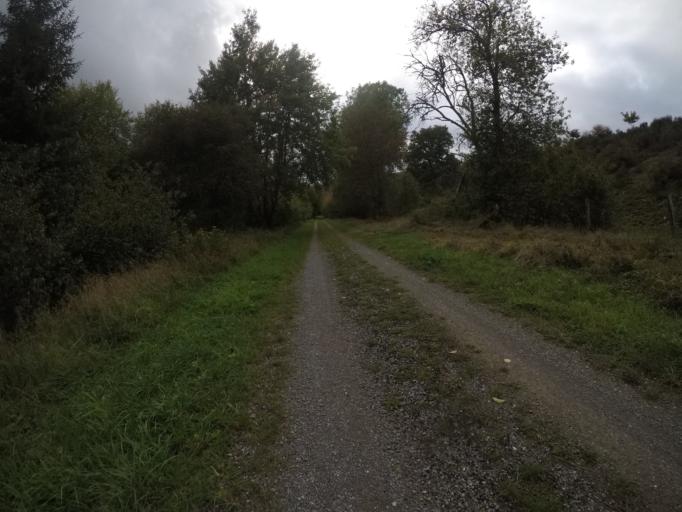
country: BE
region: Wallonia
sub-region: Province du Luxembourg
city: Fauvillers
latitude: 49.8846
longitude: 5.6755
